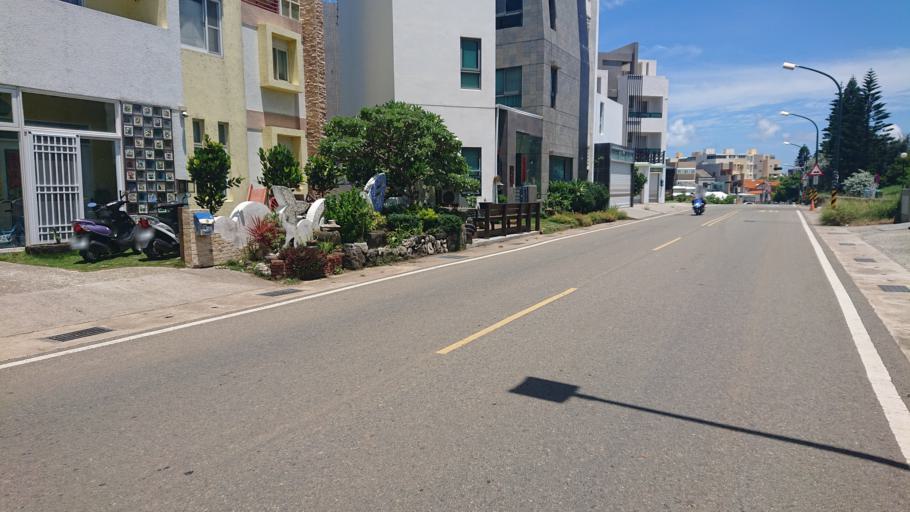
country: TW
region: Taiwan
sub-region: Penghu
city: Ma-kung
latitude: 23.5782
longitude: 119.5801
